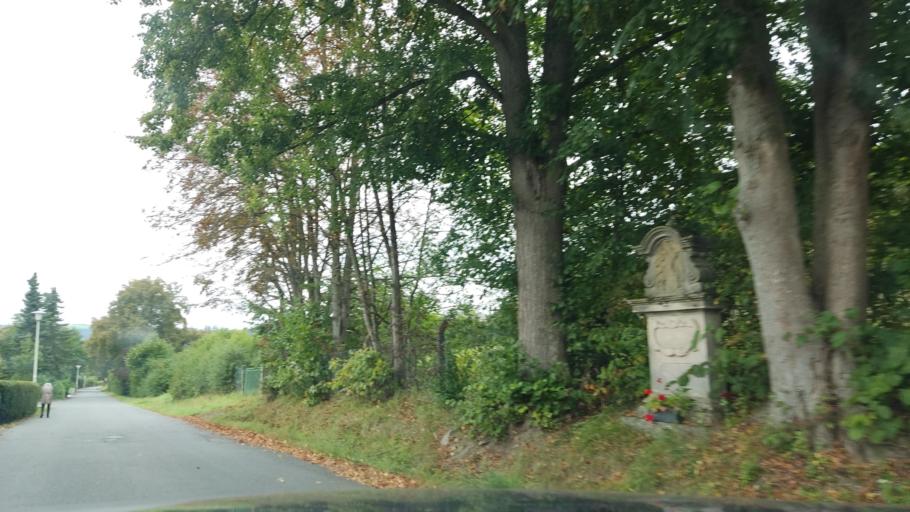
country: DE
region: Bavaria
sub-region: Upper Franconia
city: Kronach
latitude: 50.2398
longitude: 11.3492
